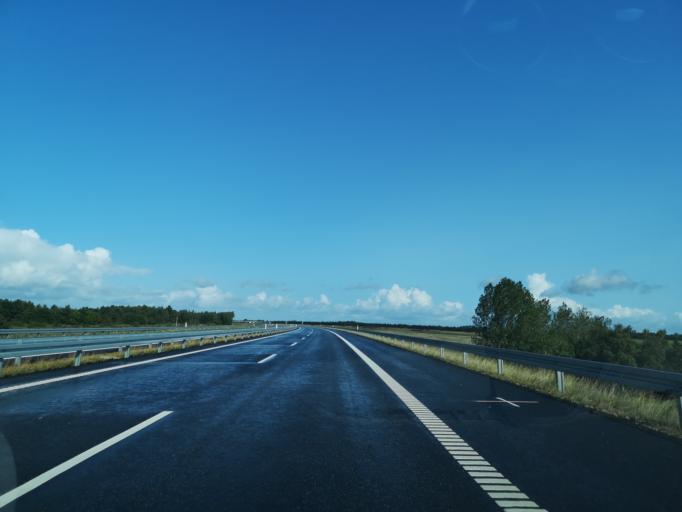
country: DK
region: Central Jutland
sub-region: Herning Kommune
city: Snejbjerg
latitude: 56.1873
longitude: 8.8911
